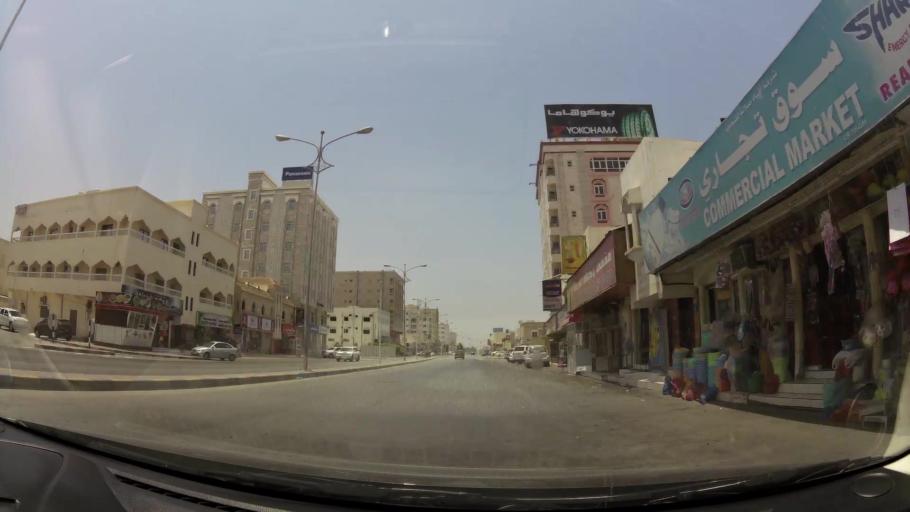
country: OM
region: Zufar
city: Salalah
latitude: 17.0187
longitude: 54.1070
